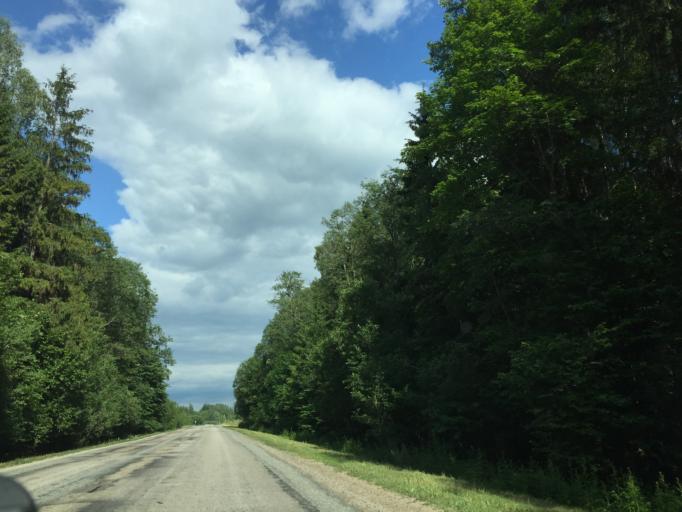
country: LV
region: Skriveri
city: Skriveri
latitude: 56.8042
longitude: 25.0879
